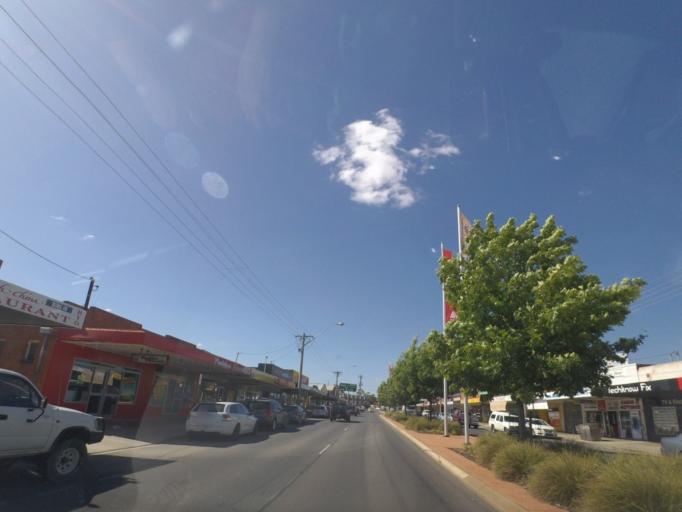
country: AU
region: New South Wales
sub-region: Albury Municipality
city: Lavington
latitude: -36.0542
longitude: 146.9332
